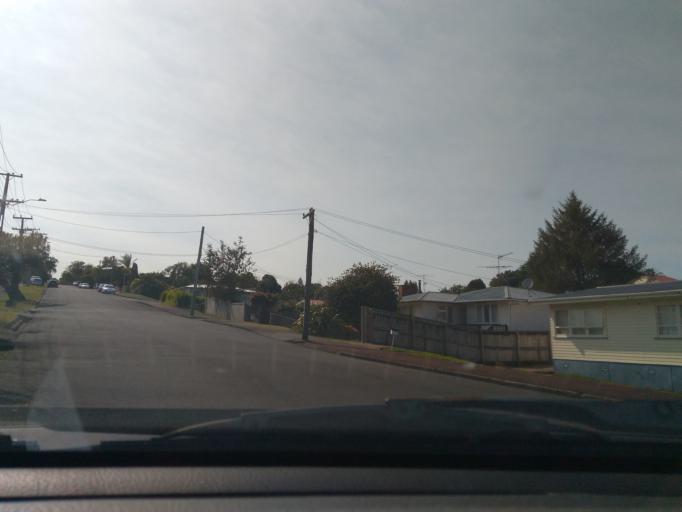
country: NZ
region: Auckland
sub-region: Auckland
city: Waitakere
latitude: -36.9222
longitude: 174.6943
